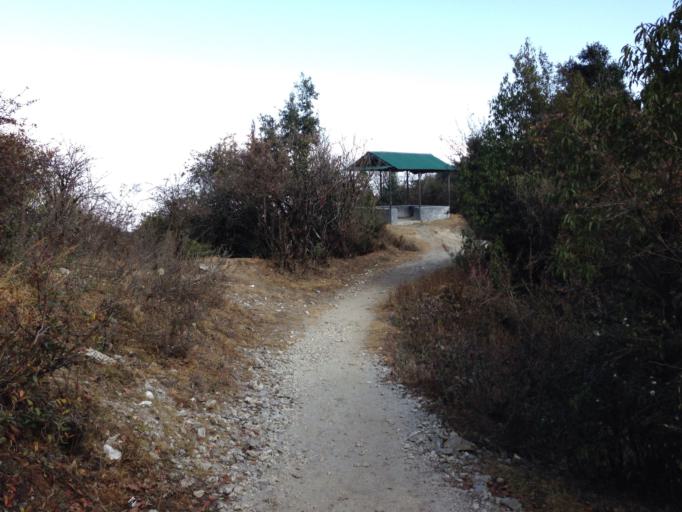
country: NP
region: Central Region
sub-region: Bagmati Zone
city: Nagarkot
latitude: 27.8142
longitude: 85.4453
